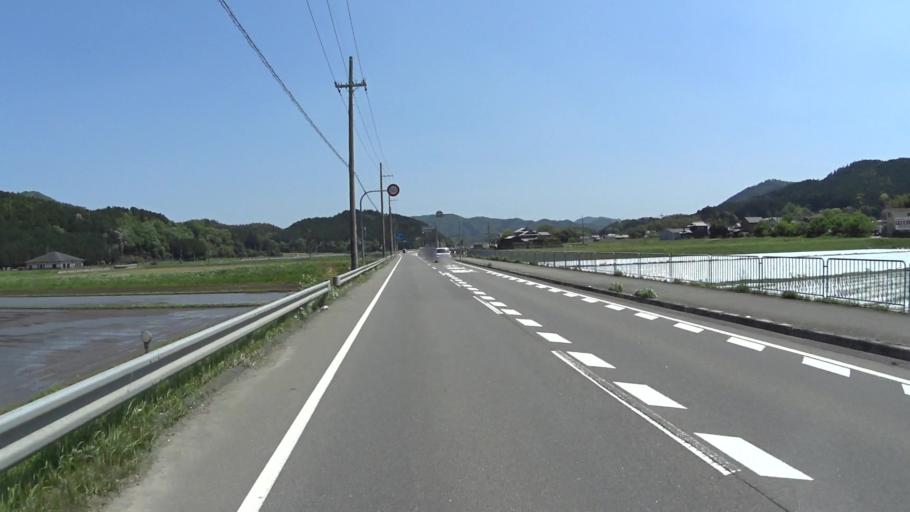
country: JP
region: Kyoto
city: Kameoka
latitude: 35.0447
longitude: 135.4805
